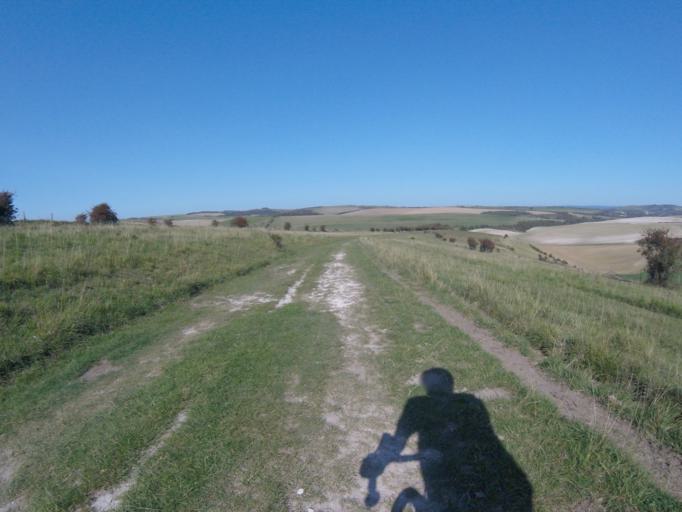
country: GB
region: England
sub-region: Brighton and Hove
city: Rottingdean
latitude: 50.8566
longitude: -0.0561
